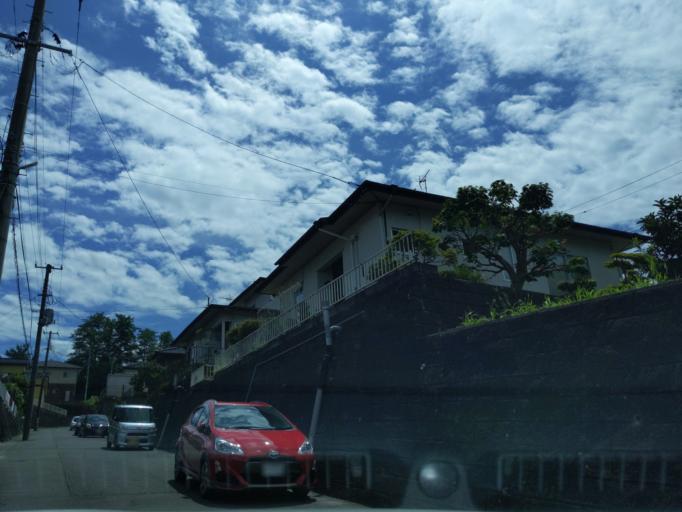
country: JP
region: Fukushima
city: Koriyama
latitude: 37.3609
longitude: 140.3523
